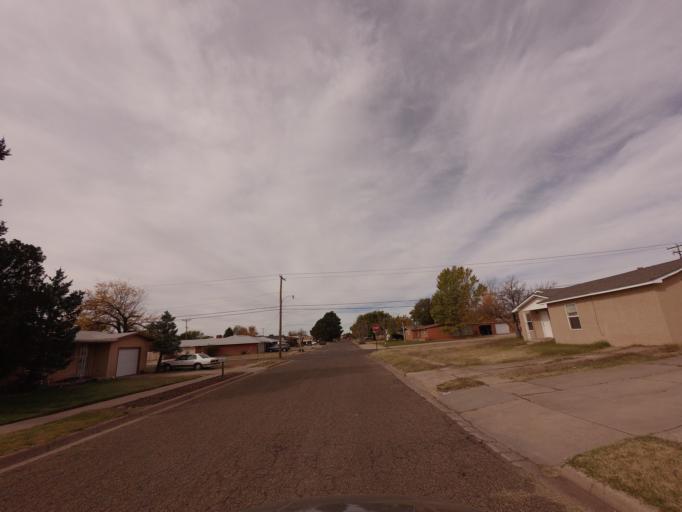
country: US
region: New Mexico
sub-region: Curry County
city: Clovis
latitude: 34.4230
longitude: -103.2137
